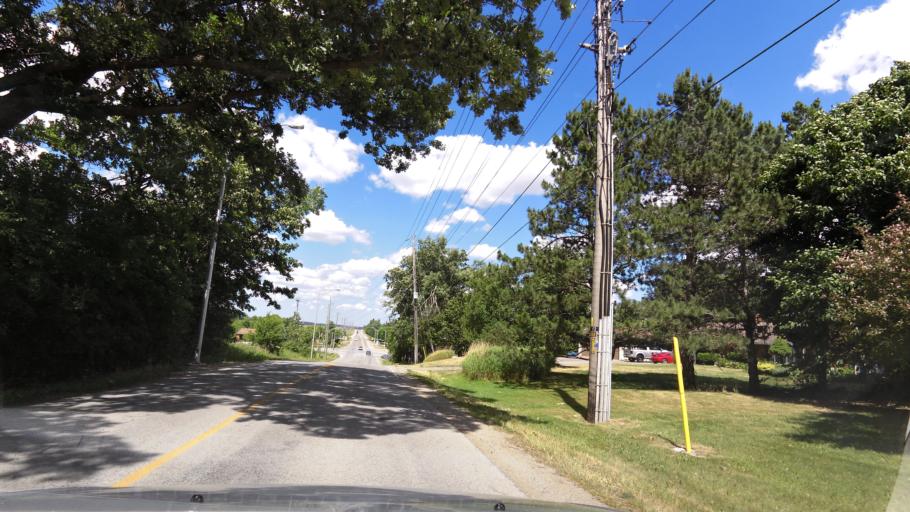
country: CA
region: Ontario
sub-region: Halton
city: Milton
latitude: 43.6067
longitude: -79.8962
